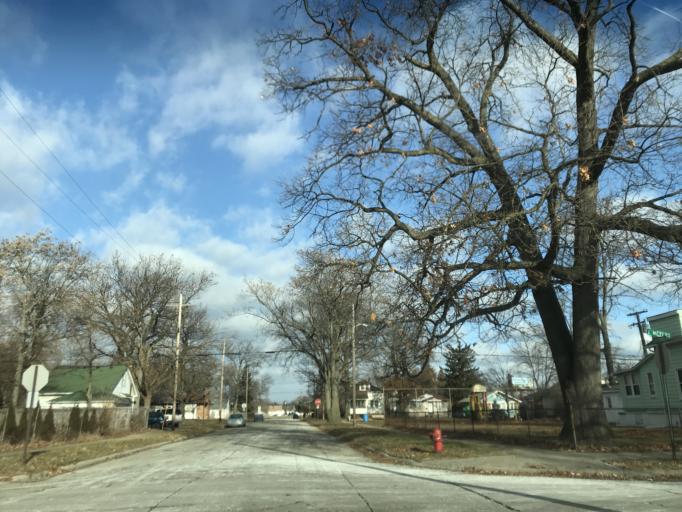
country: US
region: Michigan
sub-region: Oakland County
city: Hazel Park
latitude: 42.4545
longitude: -83.0978
